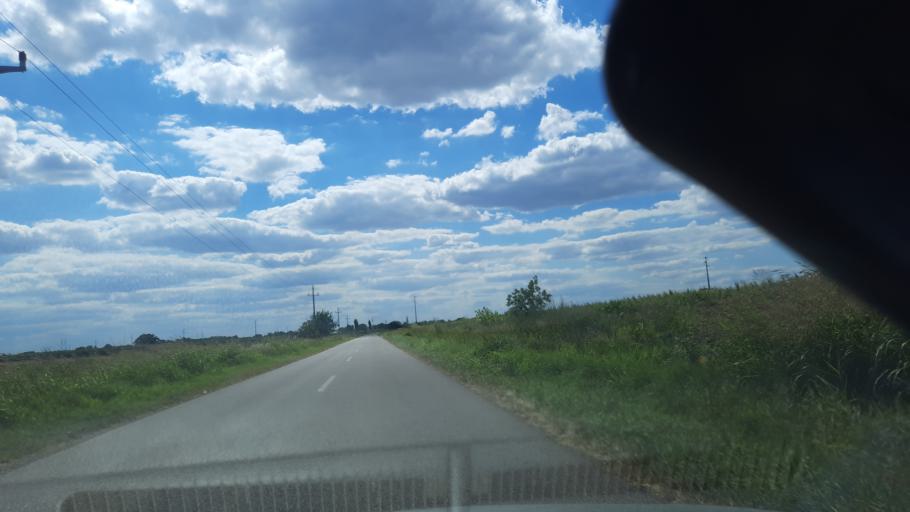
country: RS
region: Autonomna Pokrajina Vojvodina
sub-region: Sremski Okrug
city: Pecinci
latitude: 44.9070
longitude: 19.9485
